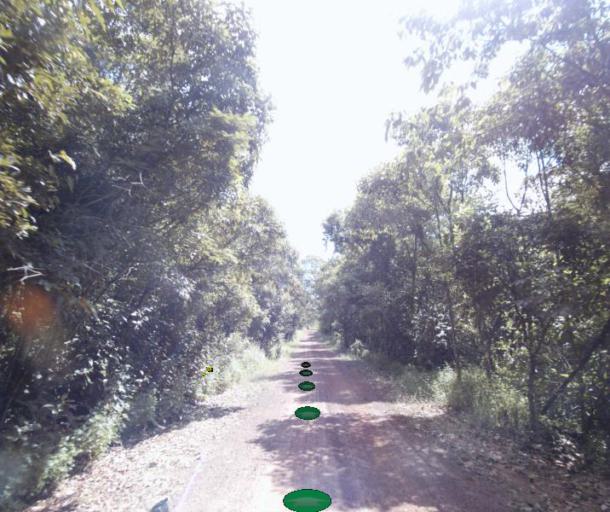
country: BR
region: Goias
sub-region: Pirenopolis
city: Pirenopolis
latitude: -15.7920
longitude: -48.8986
